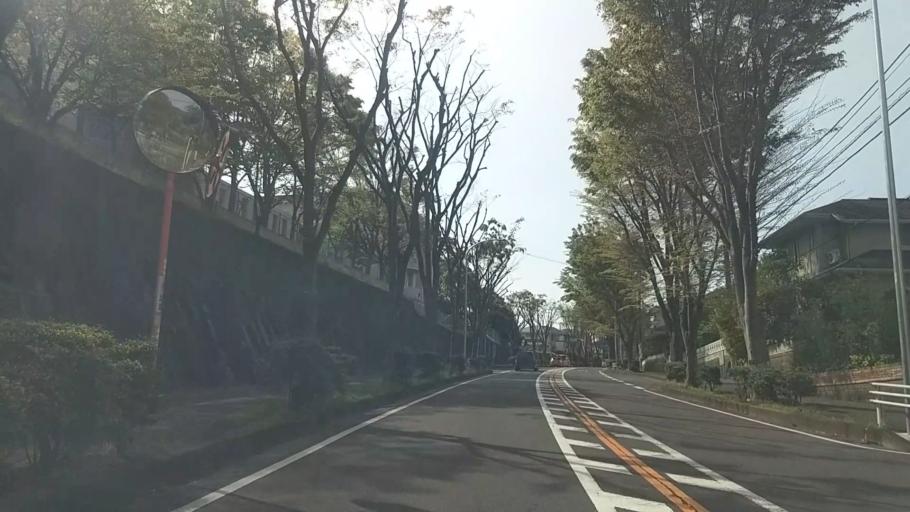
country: JP
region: Kanagawa
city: Zushi
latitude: 35.3638
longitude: 139.6106
